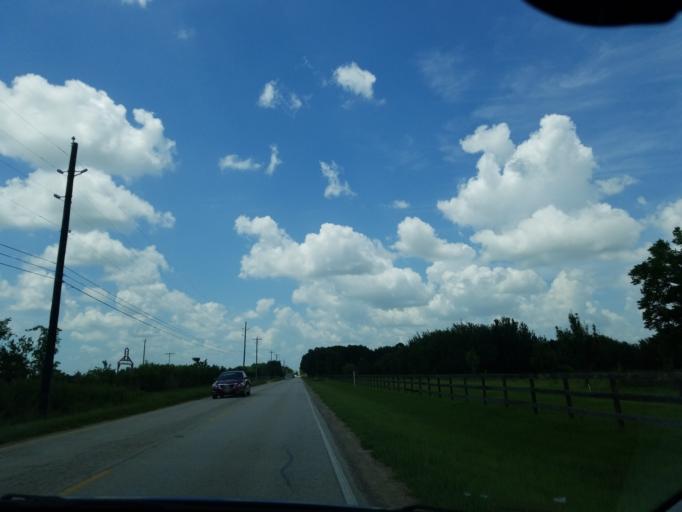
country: US
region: Texas
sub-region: Harris County
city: Katy
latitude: 29.8566
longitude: -95.8070
